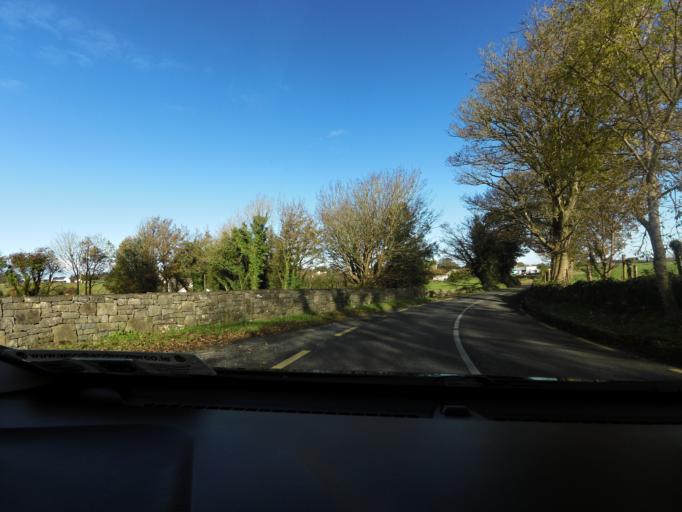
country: IE
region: Connaught
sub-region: Maigh Eo
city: Ballinrobe
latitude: 53.5164
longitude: -9.0861
